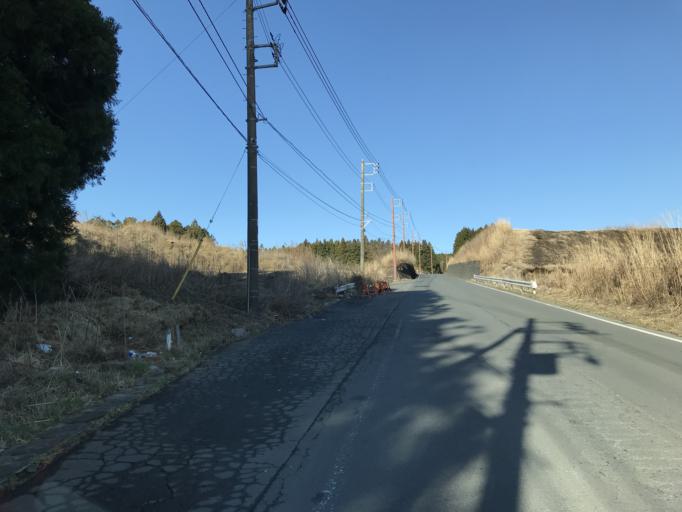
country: JP
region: Shizuoka
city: Gotemba
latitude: 35.2621
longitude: 138.8588
